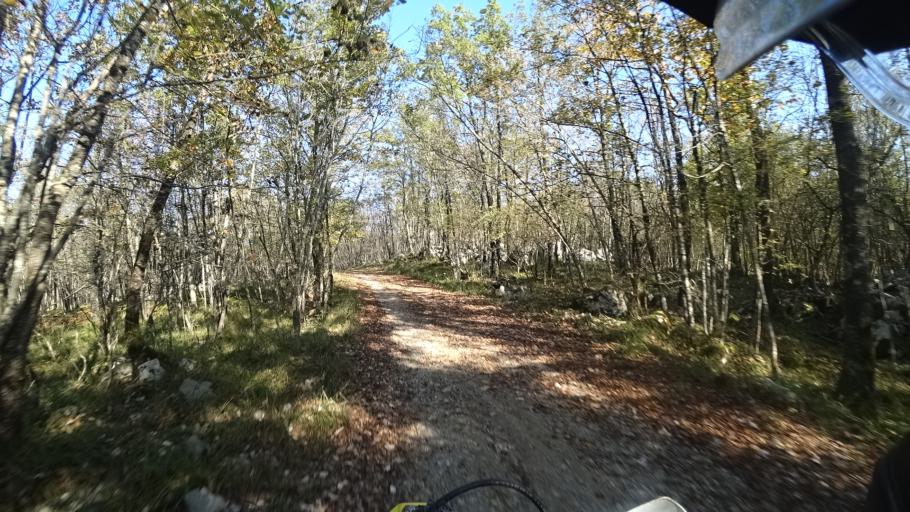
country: HR
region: Primorsko-Goranska
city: Kastav
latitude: 45.4165
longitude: 14.3396
